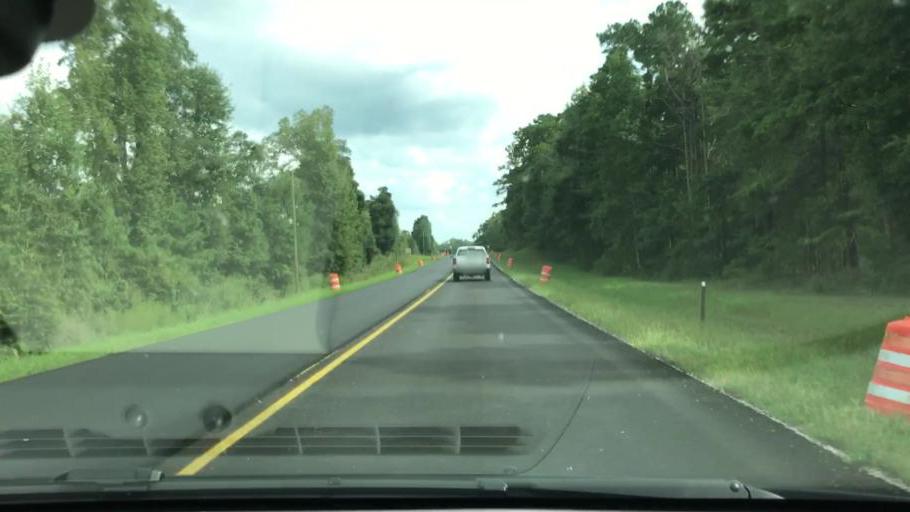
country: US
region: Georgia
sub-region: Clay County
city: Fort Gaines
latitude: 31.5866
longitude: -85.0290
